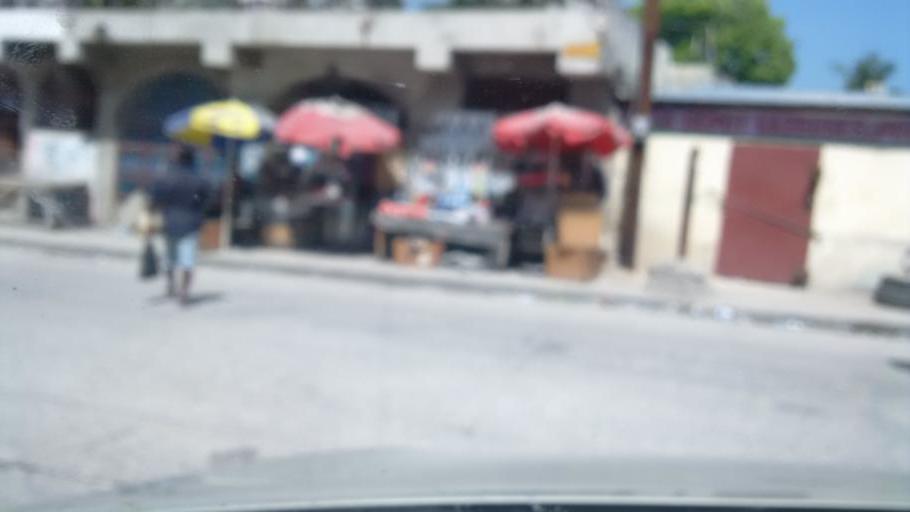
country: HT
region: Ouest
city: Delmas 73
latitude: 18.5419
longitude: -72.3172
